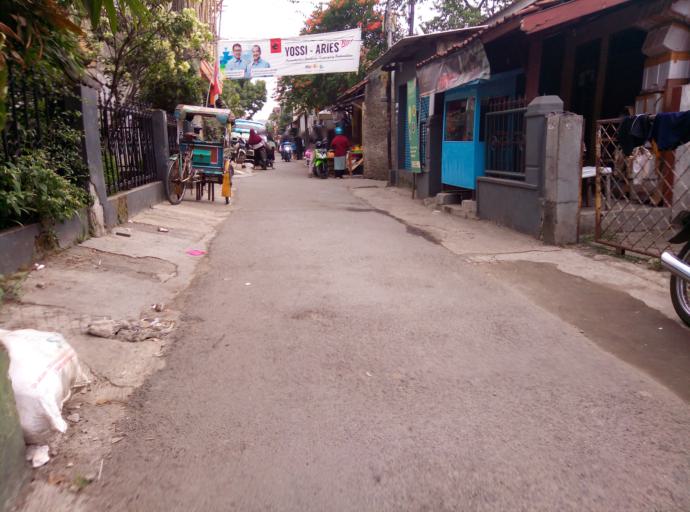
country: ID
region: West Java
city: Bandung
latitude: -6.9275
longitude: 107.6470
